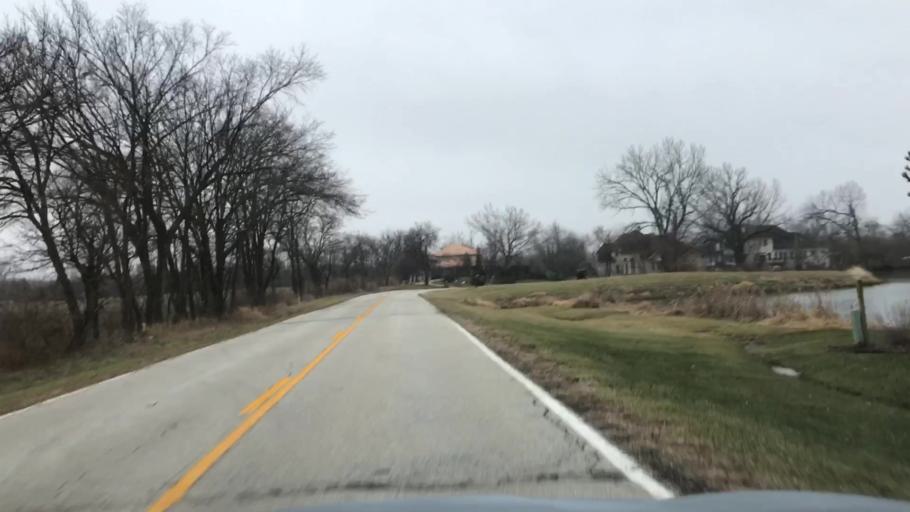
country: US
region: Illinois
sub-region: McLean County
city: Hudson
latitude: 40.6340
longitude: -88.9181
